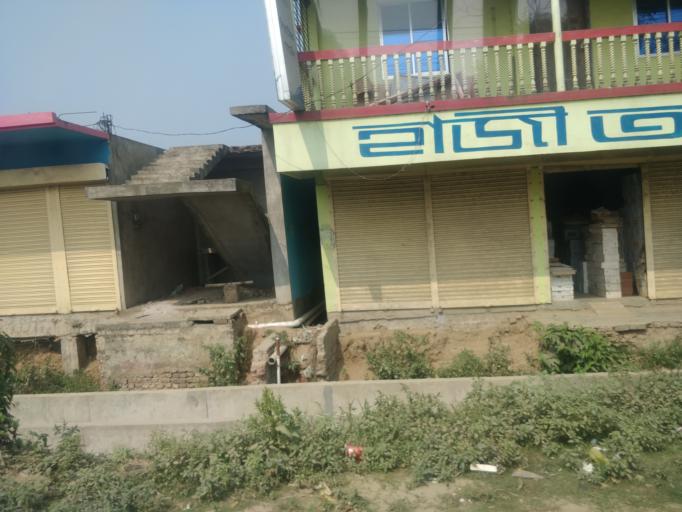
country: BD
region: Sylhet
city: Habiganj
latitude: 24.3660
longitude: 91.4156
